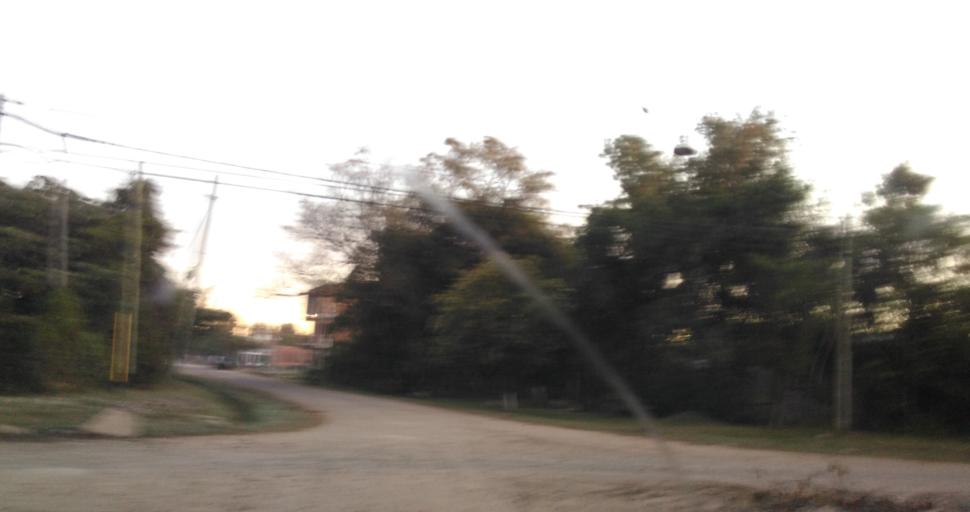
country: AR
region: Chaco
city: Resistencia
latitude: -27.4694
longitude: -58.9998
